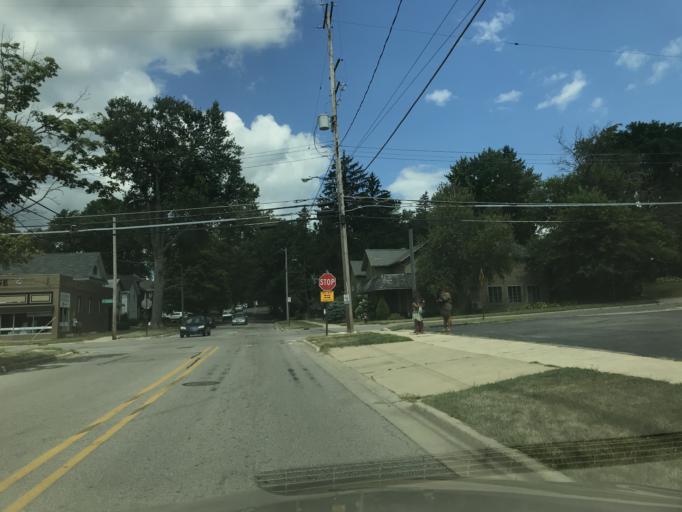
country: US
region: Michigan
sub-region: Jackson County
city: Jackson
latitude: 42.2435
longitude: -84.4185
